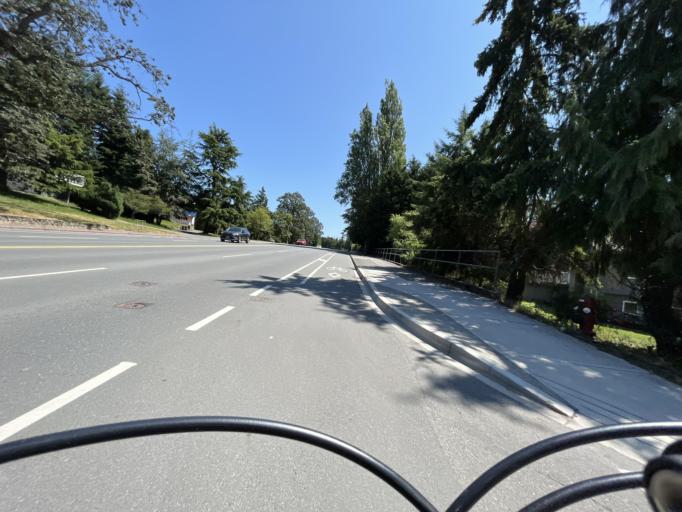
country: CA
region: British Columbia
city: Oak Bay
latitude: 48.4704
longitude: -123.3432
